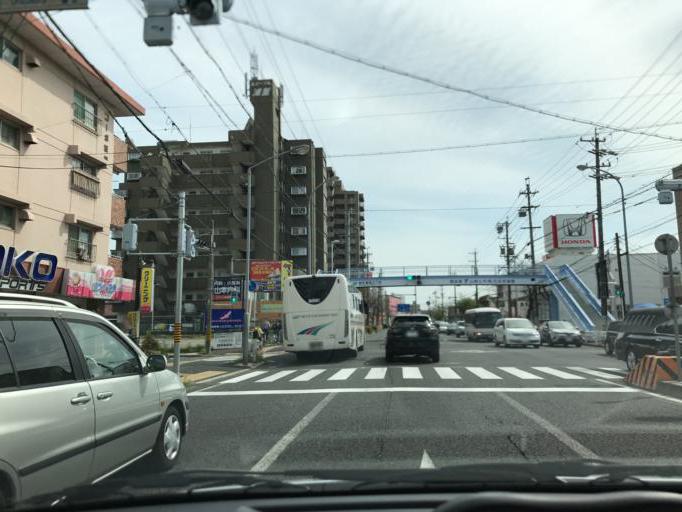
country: JP
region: Aichi
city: Obu
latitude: 35.0860
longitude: 136.9484
